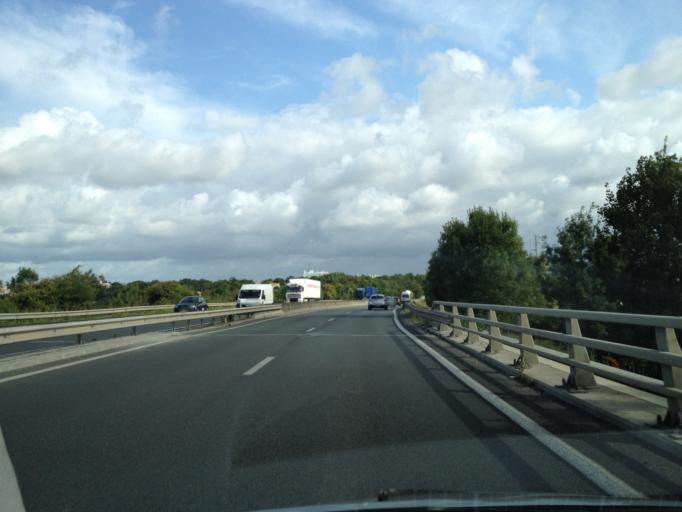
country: FR
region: Poitou-Charentes
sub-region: Departement de la Charente-Maritime
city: Puilboreau
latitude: 46.1622
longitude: -1.1218
